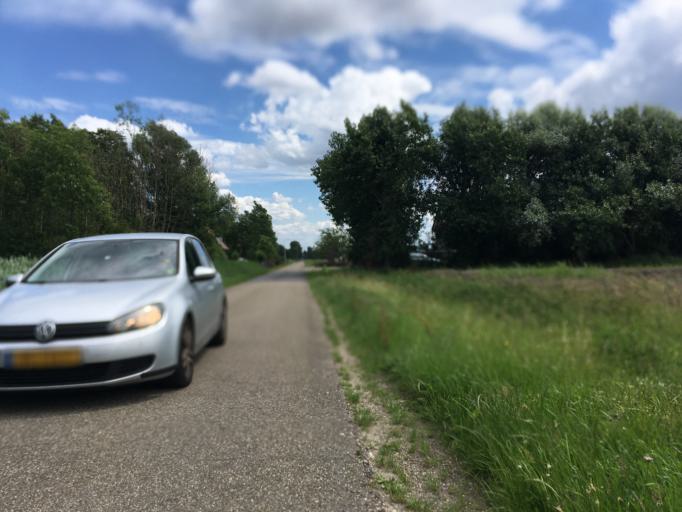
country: NL
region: North Holland
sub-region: Gemeente Velsen
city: Velsen-Zuid
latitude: 52.4253
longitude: 4.7143
